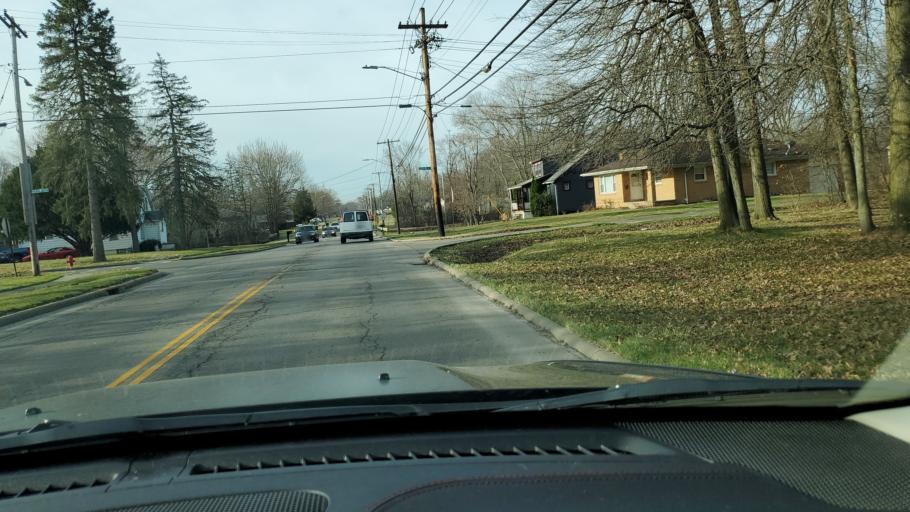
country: US
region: Ohio
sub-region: Trumbull County
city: Bolindale
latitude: 41.2001
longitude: -80.7667
